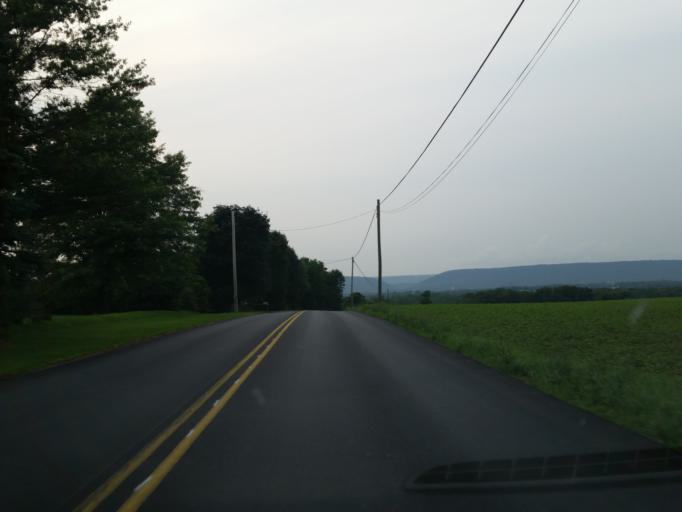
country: US
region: Pennsylvania
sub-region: Lebanon County
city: Annville
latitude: 40.3863
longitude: -76.5588
